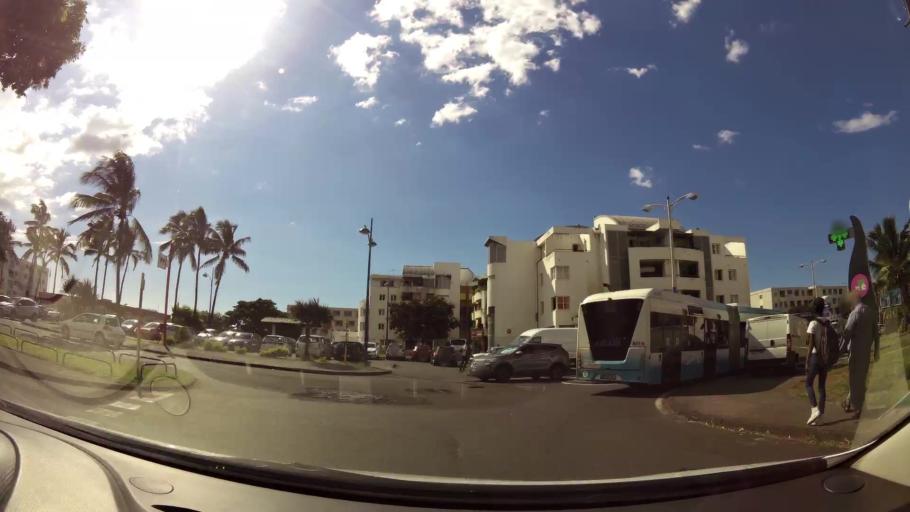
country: RE
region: Reunion
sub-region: Reunion
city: Saint-Denis
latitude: -20.8932
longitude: 55.4880
